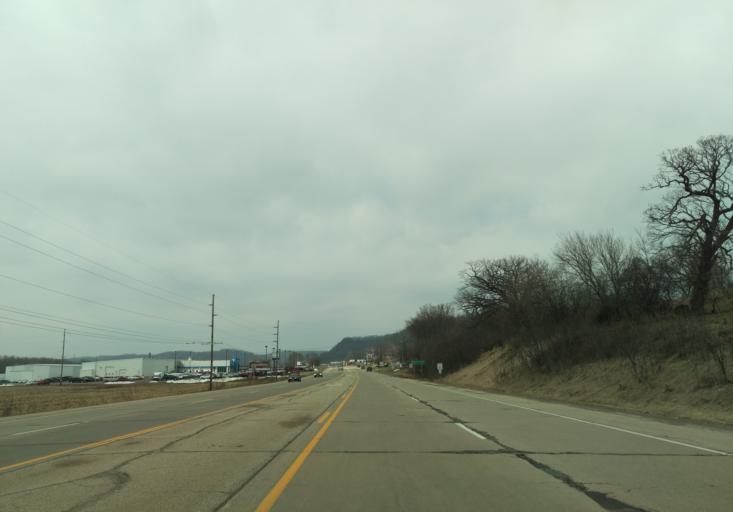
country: US
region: Wisconsin
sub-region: Richland County
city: Richland Center
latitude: 43.3166
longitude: -90.3547
